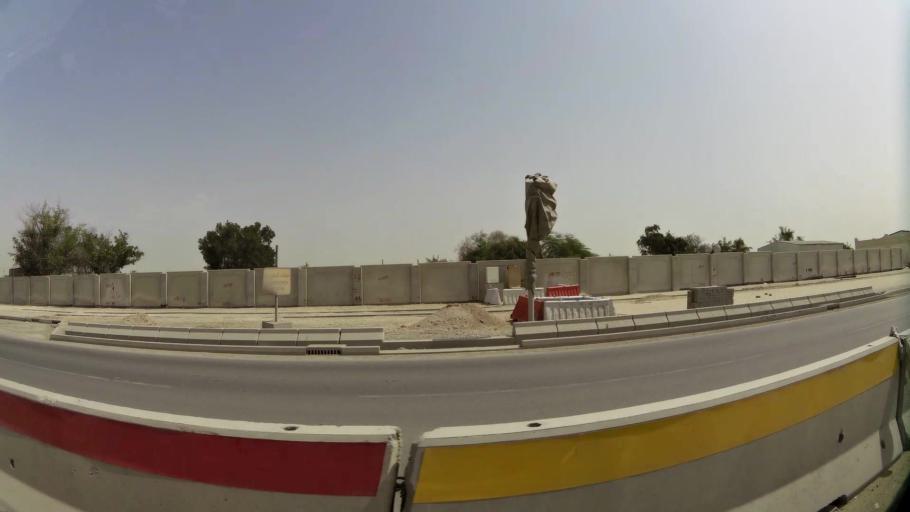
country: QA
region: Baladiyat ar Rayyan
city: Ar Rayyan
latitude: 25.1961
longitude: 51.4163
